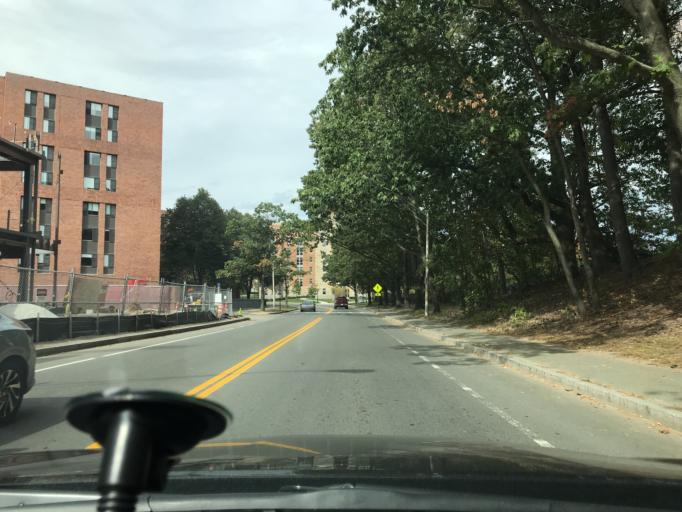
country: US
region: Massachusetts
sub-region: Middlesex County
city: Watertown
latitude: 42.3372
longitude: -71.1641
